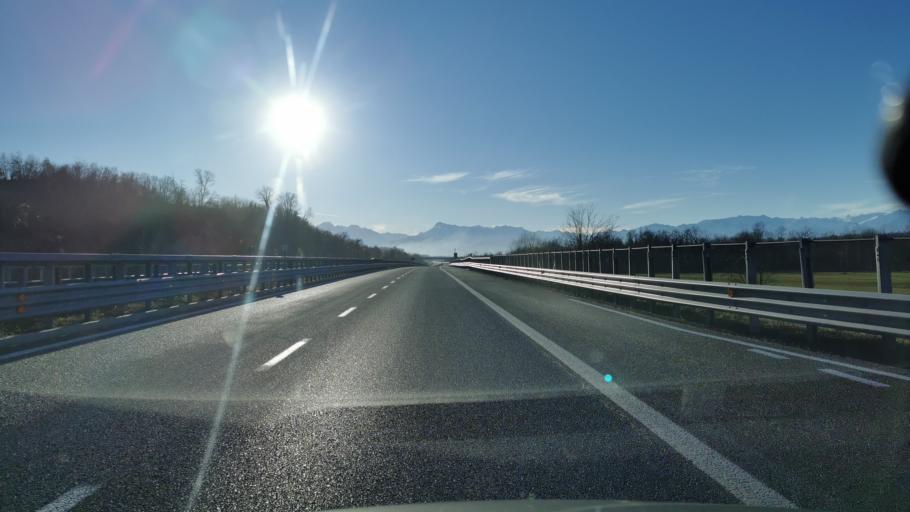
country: IT
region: Piedmont
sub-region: Provincia di Cuneo
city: Castelletto Stura
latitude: 44.4535
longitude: 7.6490
